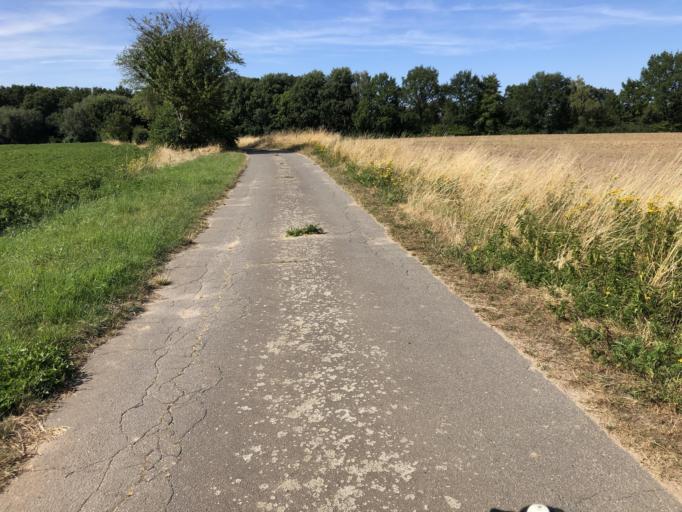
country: DE
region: Lower Saxony
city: Thomasburg
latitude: 53.1983
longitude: 10.6840
